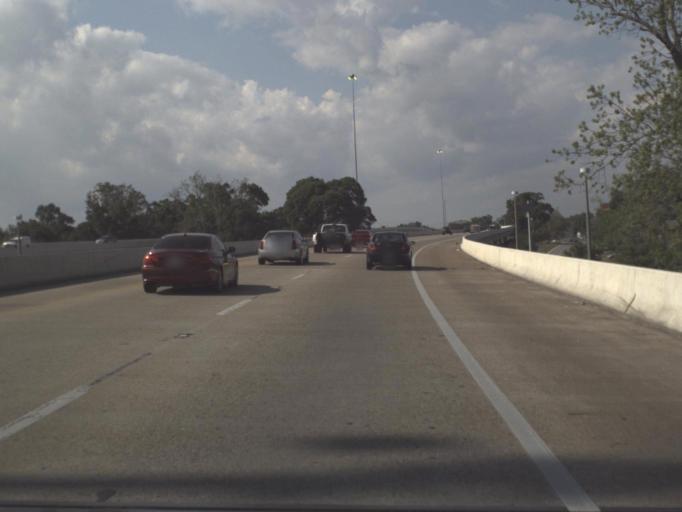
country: US
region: Florida
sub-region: Escambia County
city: Pensacola
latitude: 30.4304
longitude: -87.2154
